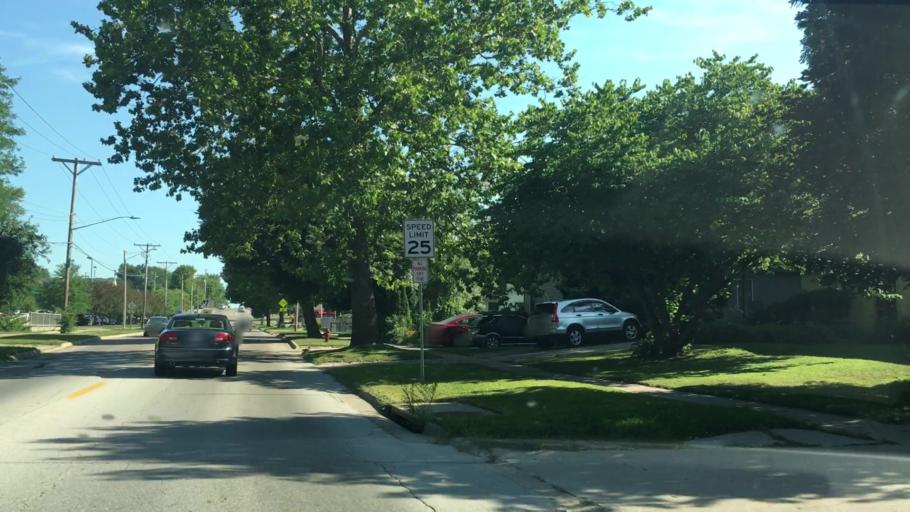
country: US
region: Iowa
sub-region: Johnson County
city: Iowa City
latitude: 41.6526
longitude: -91.5020
